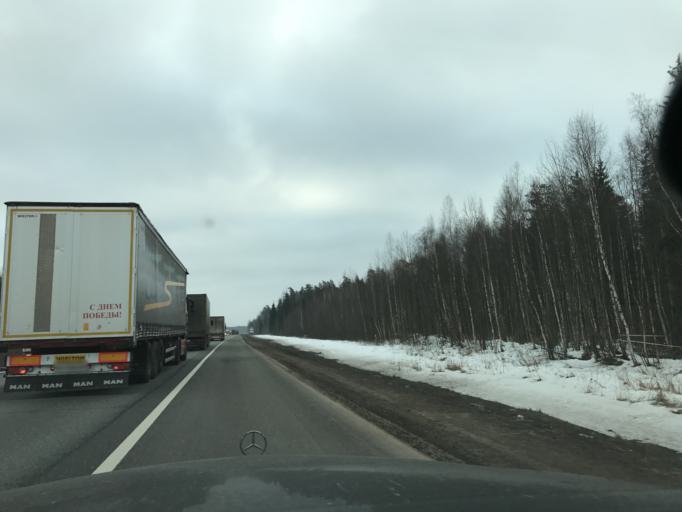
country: RU
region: Vladimir
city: Raduzhnyy
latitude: 56.0711
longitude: 40.2858
